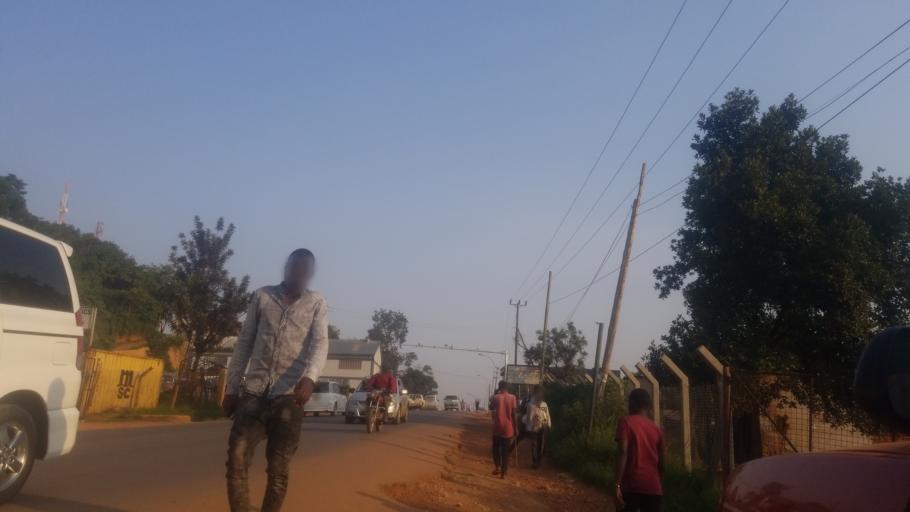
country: UG
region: Central Region
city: Kampala Central Division
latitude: 0.3414
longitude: 32.5631
